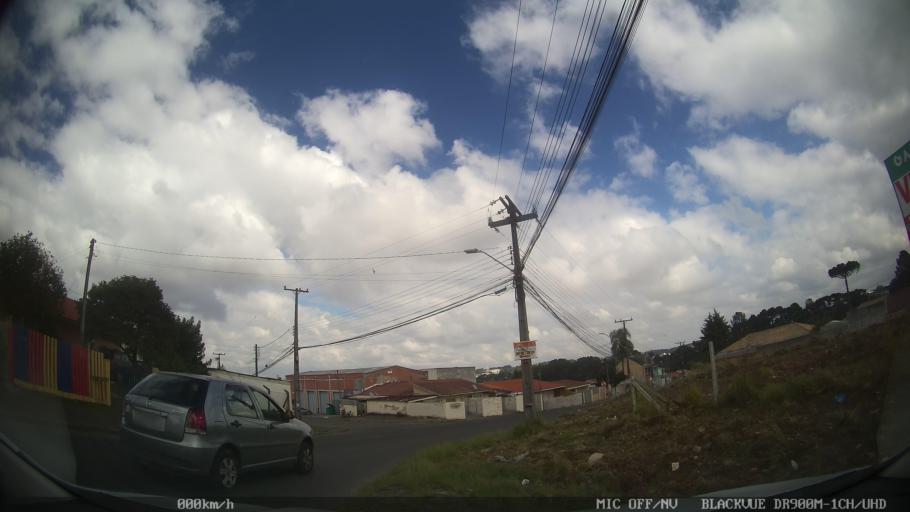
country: BR
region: Parana
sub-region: Colombo
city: Colombo
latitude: -25.3560
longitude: -49.2087
